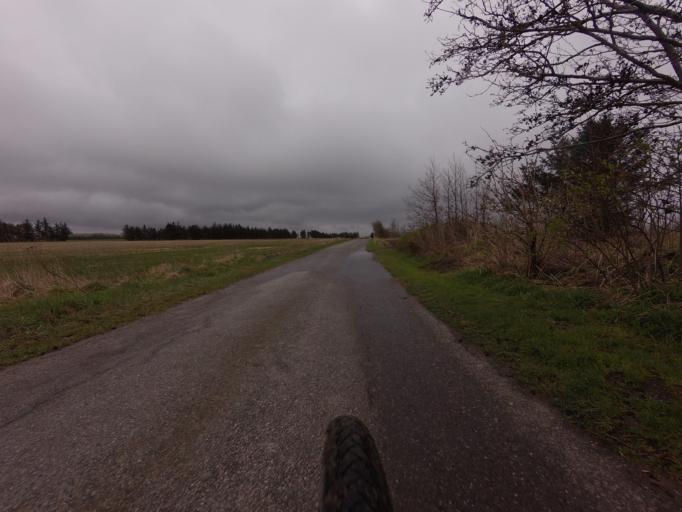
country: DK
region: North Denmark
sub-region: Jammerbugt Kommune
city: Pandrup
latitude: 57.3315
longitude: 9.7873
